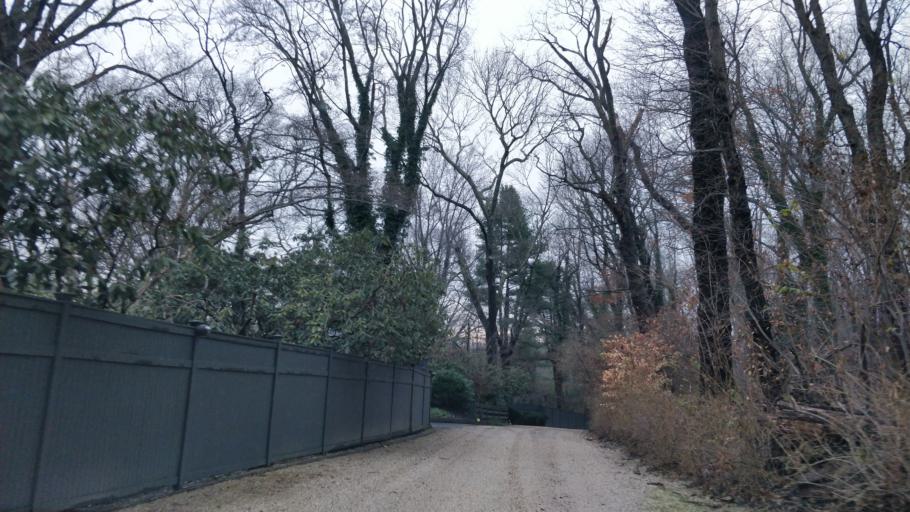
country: US
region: New York
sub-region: Nassau County
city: Upper Brookville
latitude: 40.8583
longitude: -73.5723
